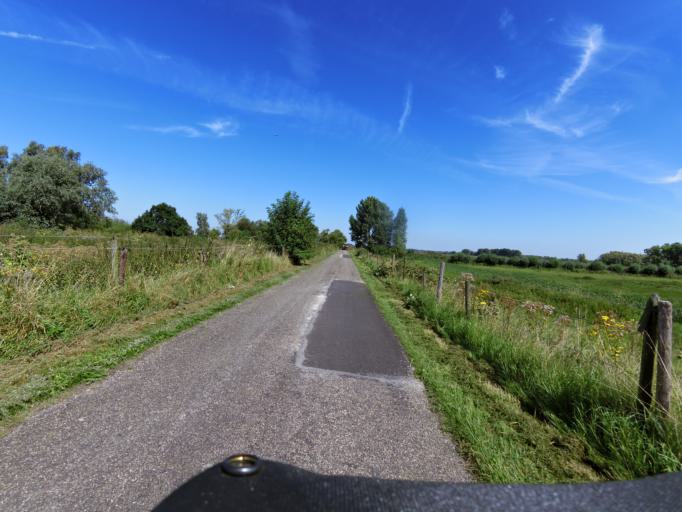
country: NL
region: South Holland
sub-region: Gemeente Dordrecht
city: Dordrecht
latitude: 51.7419
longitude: 4.7234
